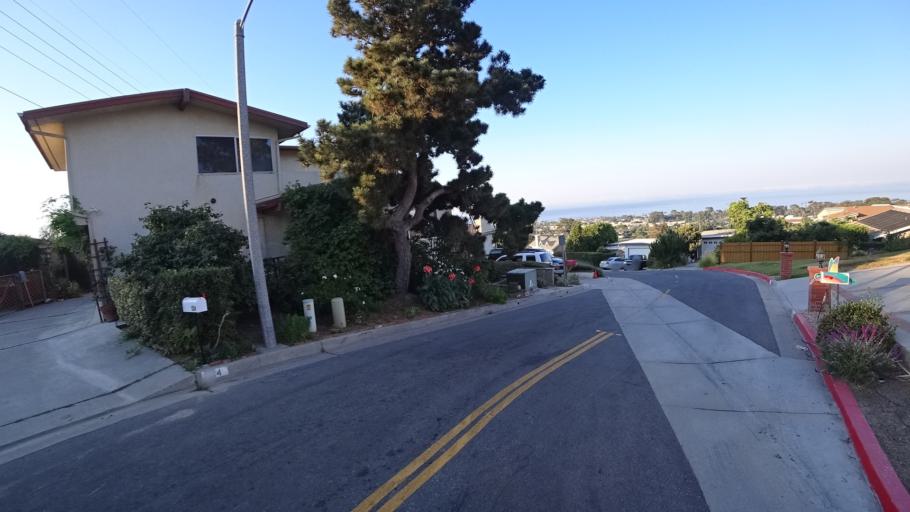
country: US
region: California
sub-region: Orange County
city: San Clemente
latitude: 33.4072
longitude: -117.5911
